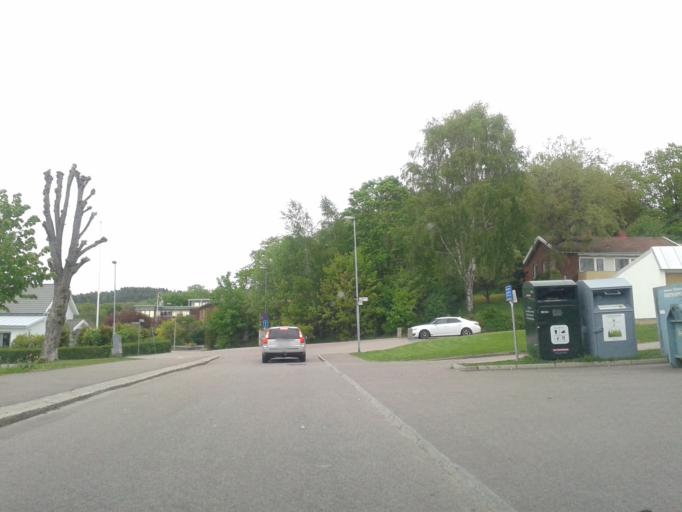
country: SE
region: Vaestra Goetaland
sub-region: Kungalvs Kommun
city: Kungalv
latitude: 57.8766
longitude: 11.9872
